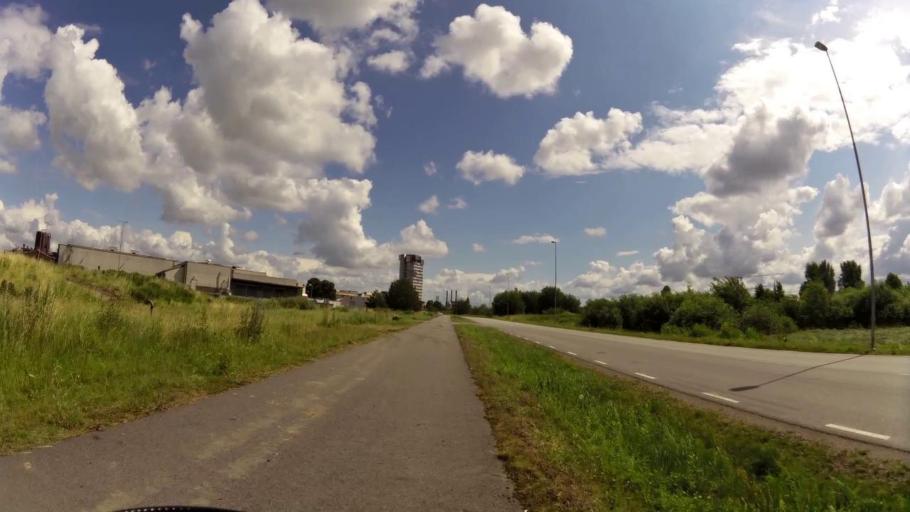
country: SE
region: OEstergoetland
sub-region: Linkopings Kommun
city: Linkoping
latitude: 58.4238
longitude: 15.6080
